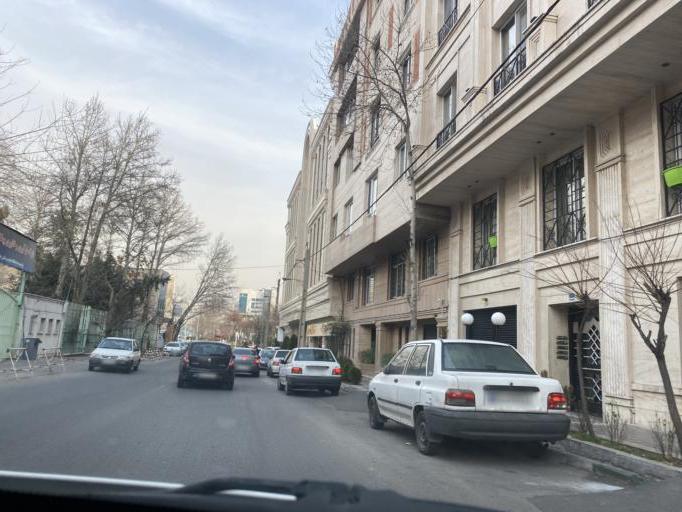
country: IR
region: Tehran
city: Tajrish
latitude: 35.8024
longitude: 51.4855
